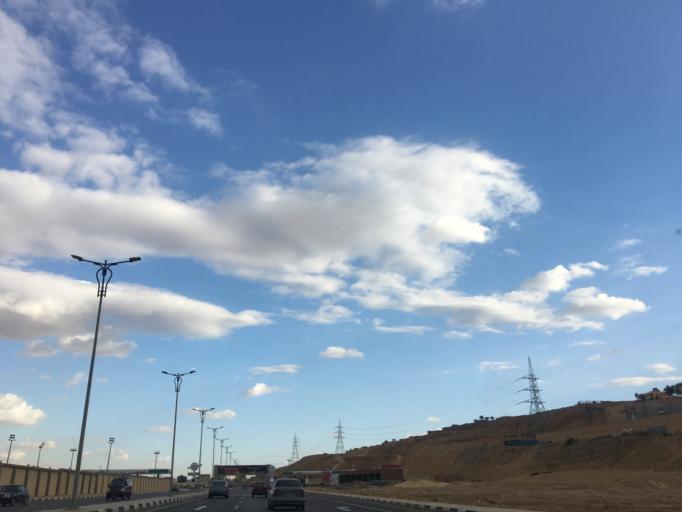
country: EG
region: Muhafazat al Qahirah
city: Cairo
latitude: 30.0230
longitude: 31.3267
